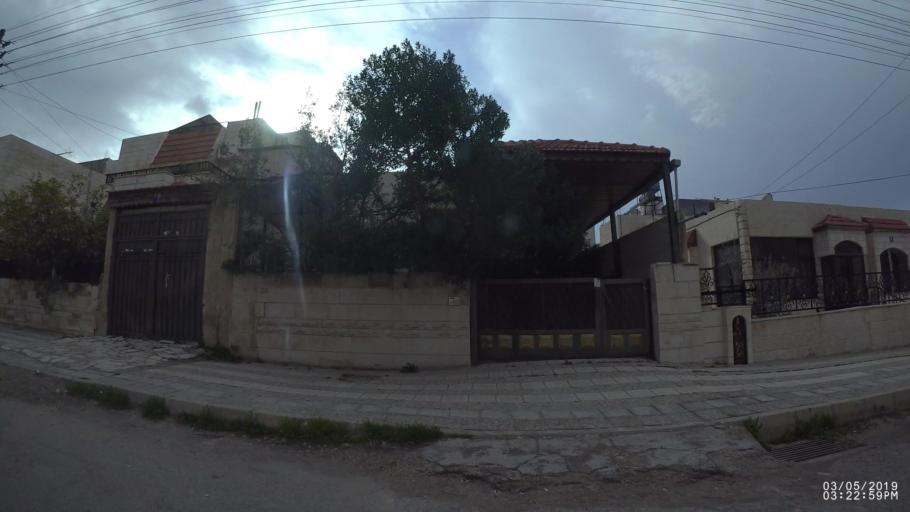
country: JO
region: Amman
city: Amman
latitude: 32.0017
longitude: 35.9439
